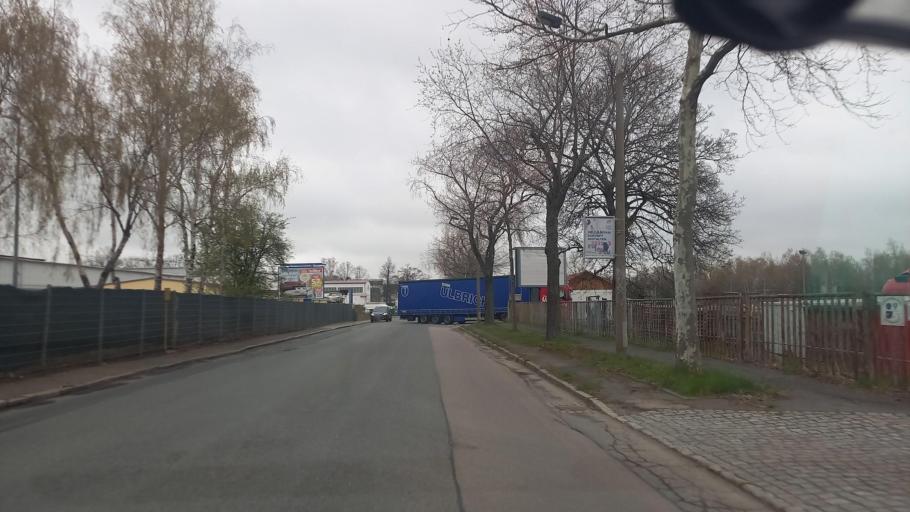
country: DE
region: Saxony
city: Zwickau
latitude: 50.7104
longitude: 12.4804
